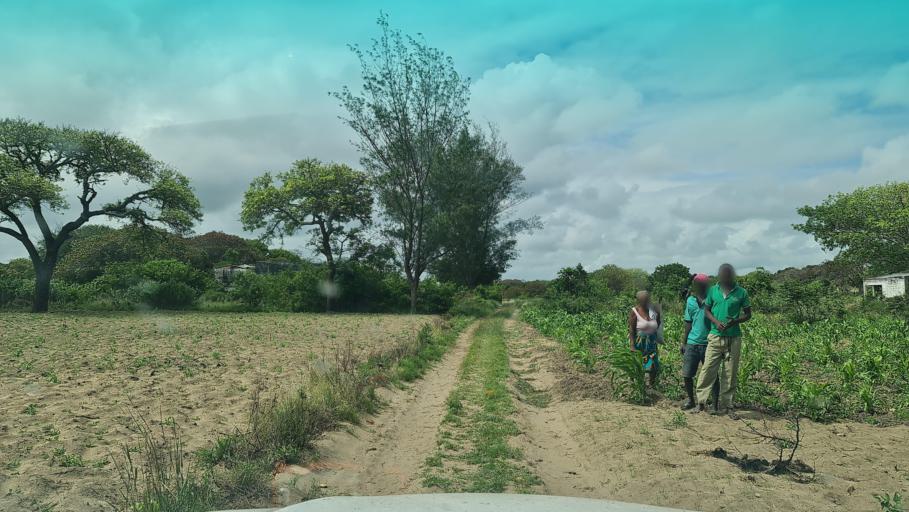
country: EG
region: Aswan
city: Idfu
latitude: 25.3970
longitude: 33.0280
